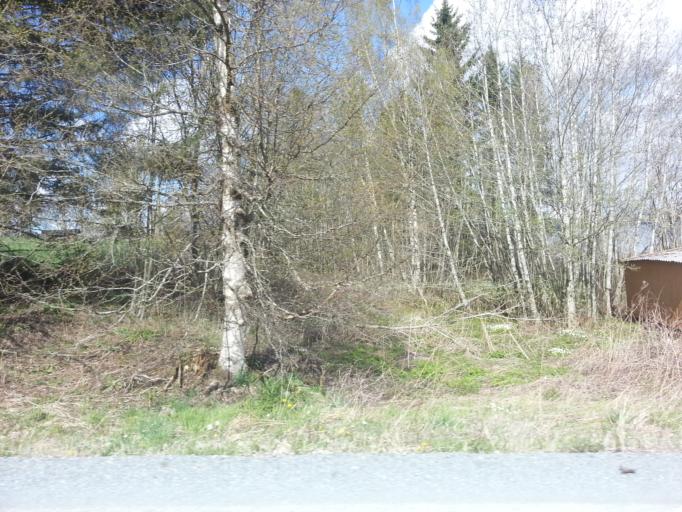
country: NO
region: Nord-Trondelag
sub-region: Levanger
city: Skogn
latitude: 63.6135
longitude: 11.1445
